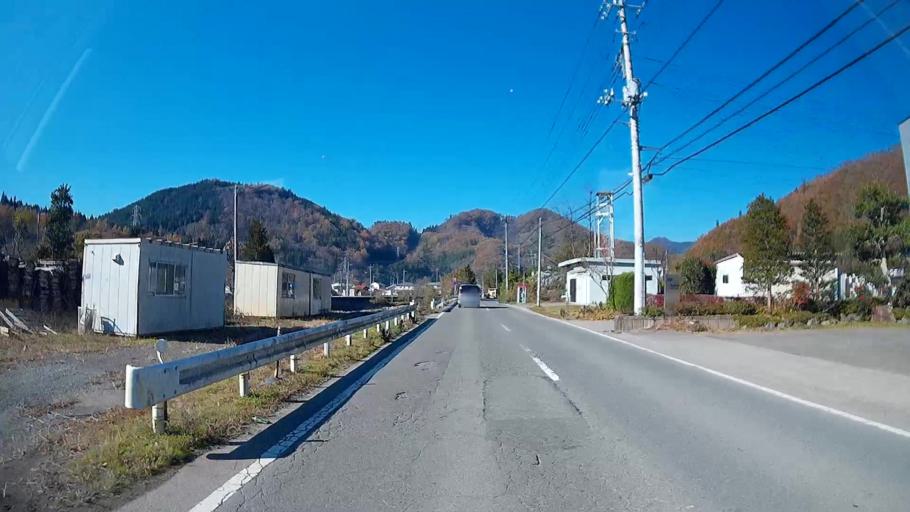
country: JP
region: Yamanashi
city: Otsuki
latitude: 35.5619
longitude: 138.9435
